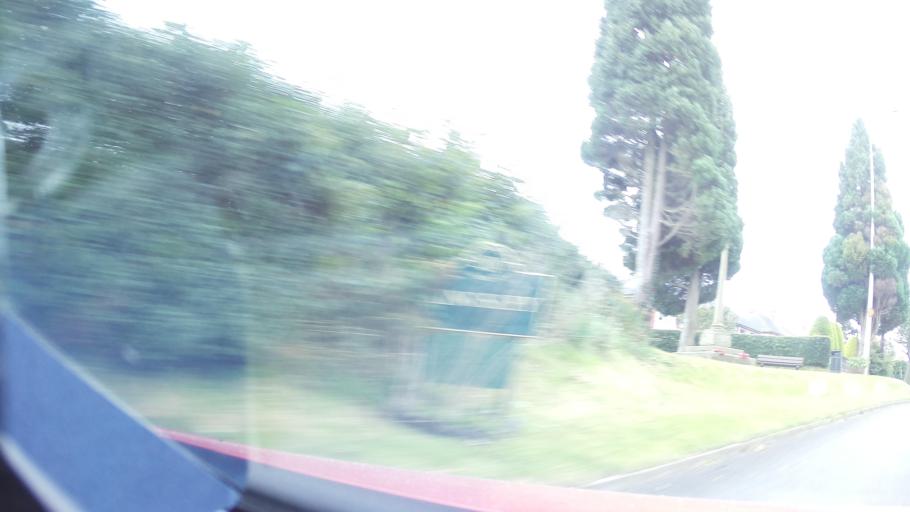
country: GB
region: England
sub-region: Staffordshire
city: Cheadle
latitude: 53.0195
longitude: -1.9798
